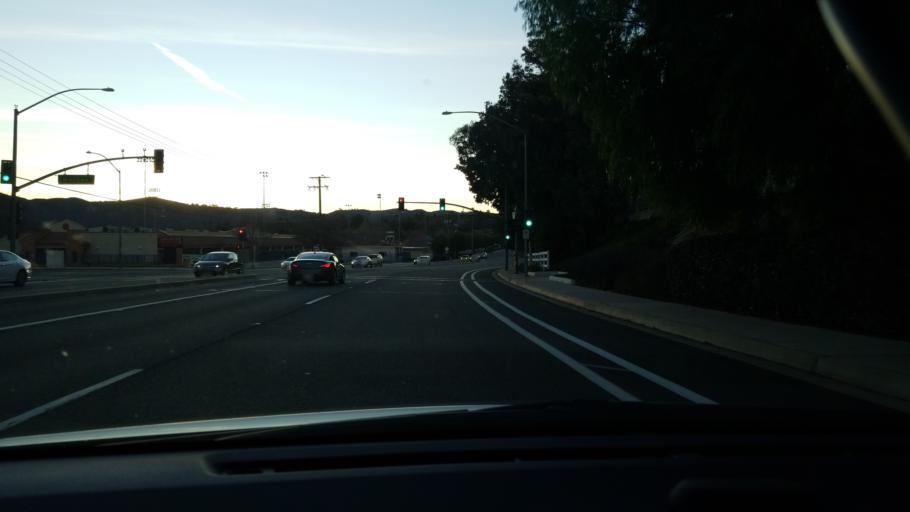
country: US
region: California
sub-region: Riverside County
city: Temecula
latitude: 33.5116
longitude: -117.1402
